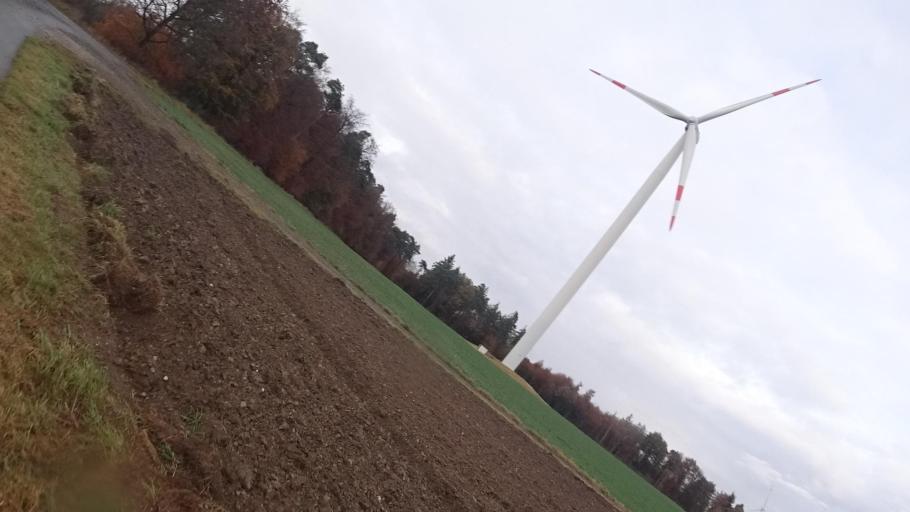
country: DE
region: Rheinland-Pfalz
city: Bickenbach
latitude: 50.1130
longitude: 7.5248
